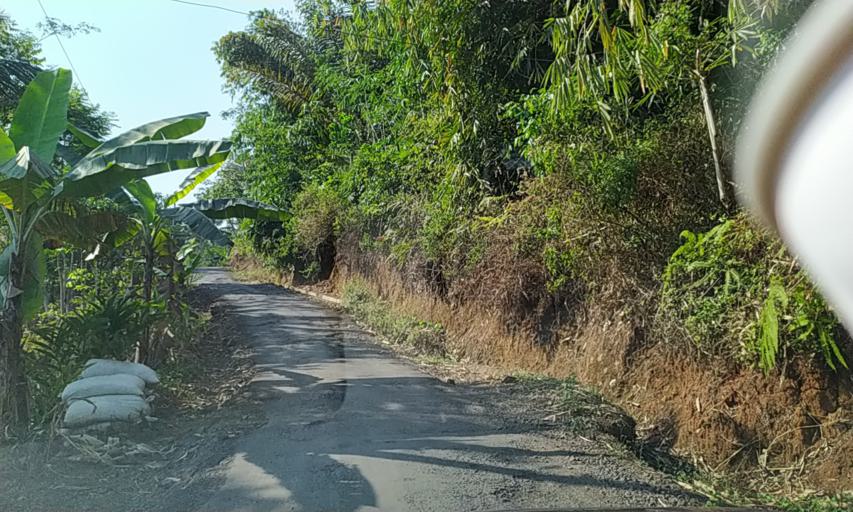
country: ID
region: Central Java
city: Datar
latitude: -7.2137
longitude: 108.6301
